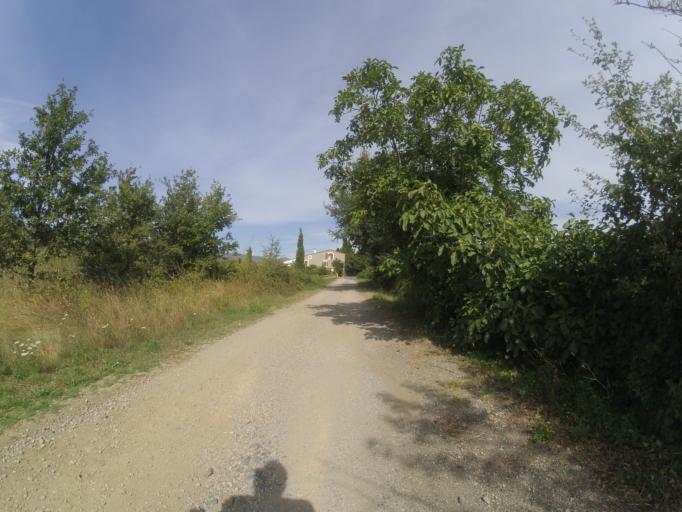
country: FR
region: Languedoc-Roussillon
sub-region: Departement des Pyrenees-Orientales
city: Ille-sur-Tet
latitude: 42.6595
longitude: 2.6285
